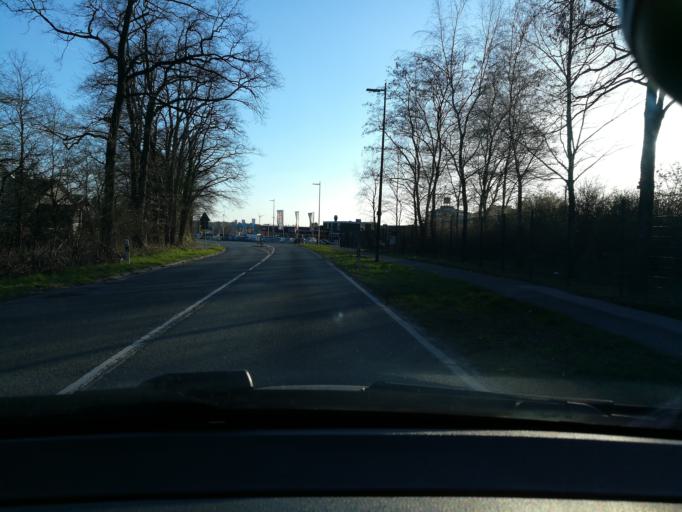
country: DE
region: North Rhine-Westphalia
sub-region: Regierungsbezirk Detmold
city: Oerlinghausen
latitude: 51.9546
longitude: 8.5786
